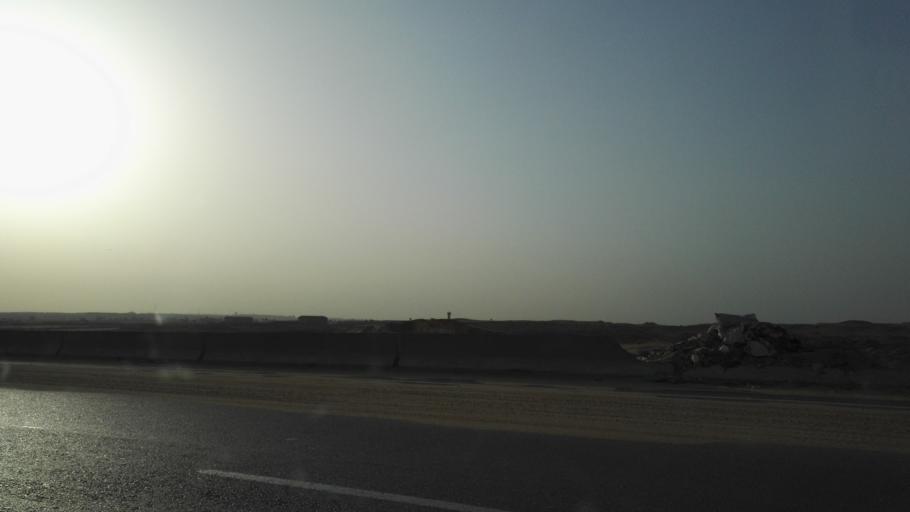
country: EG
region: Muhafazat al Qahirah
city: Cairo
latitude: 29.9920
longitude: 31.3778
